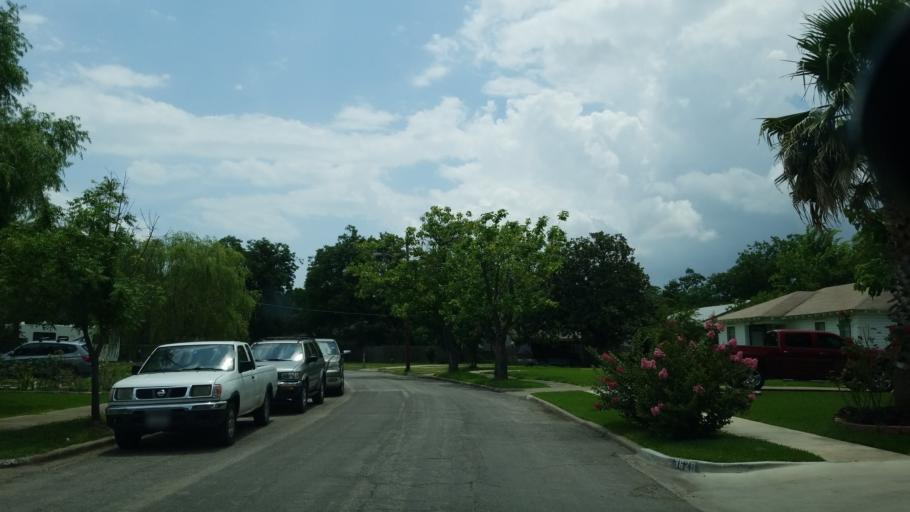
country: US
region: Texas
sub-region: Dallas County
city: Farmers Branch
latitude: 32.8759
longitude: -96.8585
